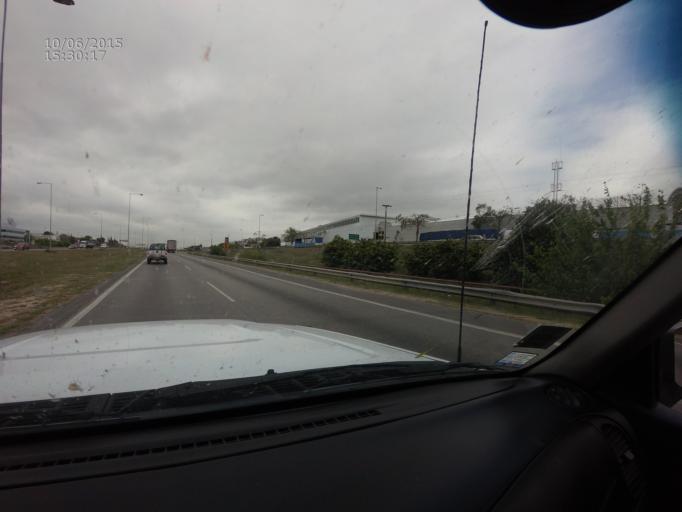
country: AR
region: Cordoba
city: Malvinas Argentinas
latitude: -31.3861
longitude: -64.1263
